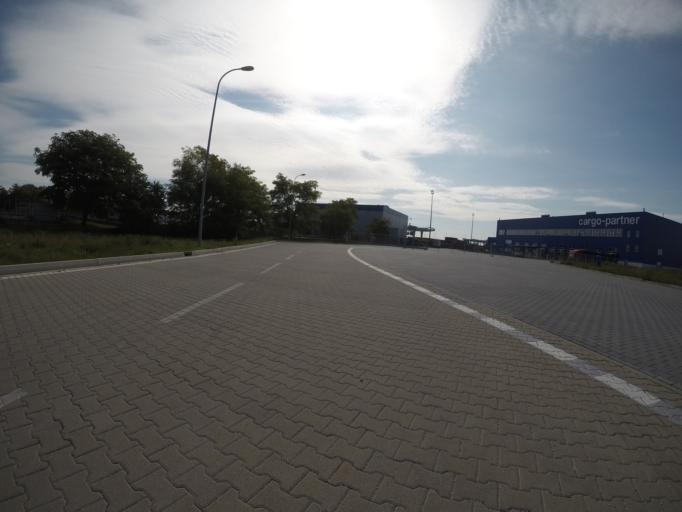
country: SK
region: Trnavsky
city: Dunajska Streda
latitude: 47.9858
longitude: 17.6261
